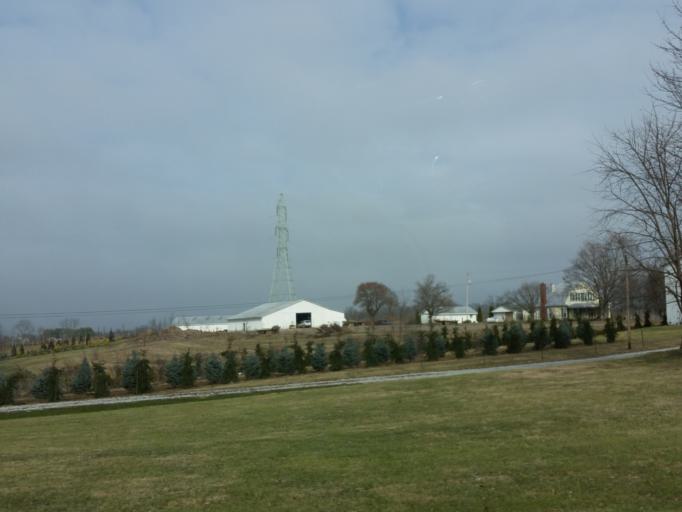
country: US
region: Indiana
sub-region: Jefferson County
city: Madison
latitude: 38.6890
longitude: -85.3476
